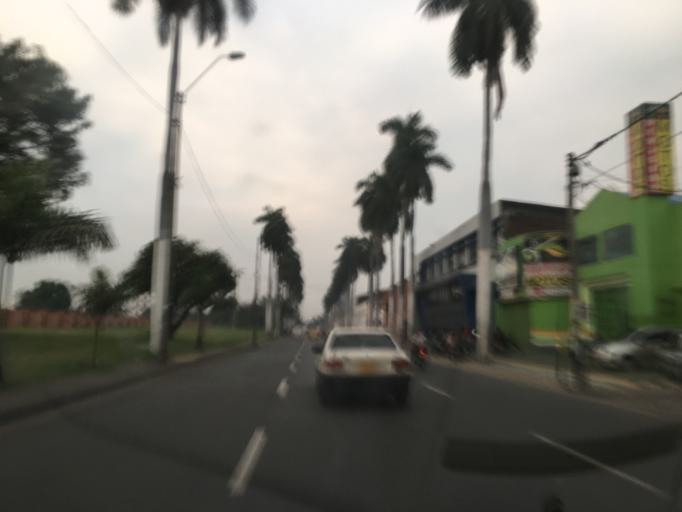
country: CO
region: Valle del Cauca
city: Cali
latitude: 3.4568
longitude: -76.5202
